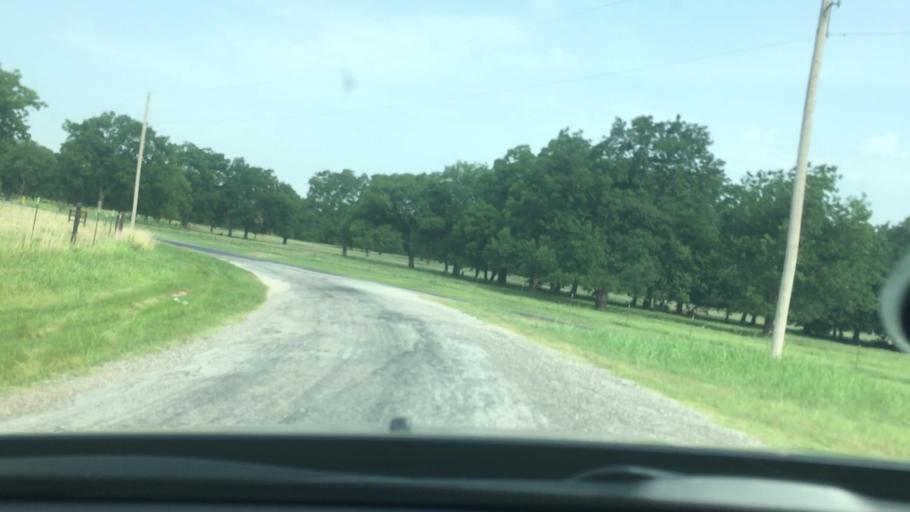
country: US
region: Oklahoma
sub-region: Garvin County
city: Pauls Valley
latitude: 34.8256
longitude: -97.1959
